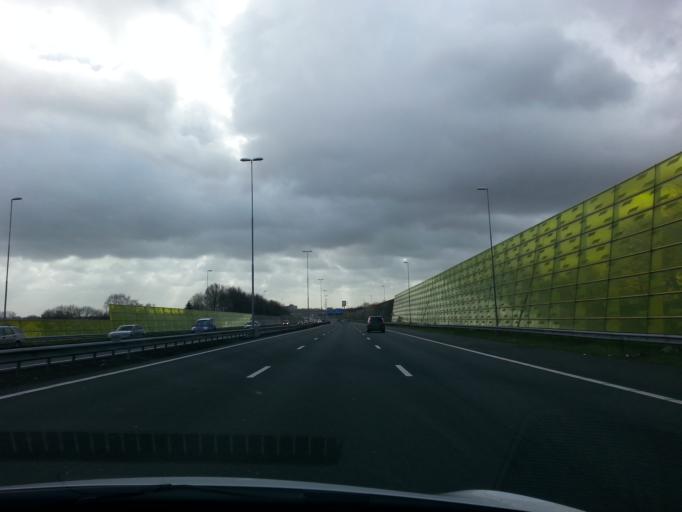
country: NL
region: North Brabant
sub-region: Gemeente 's-Hertogenbosch
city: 's-Hertogenbosch
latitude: 51.7361
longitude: 5.3070
